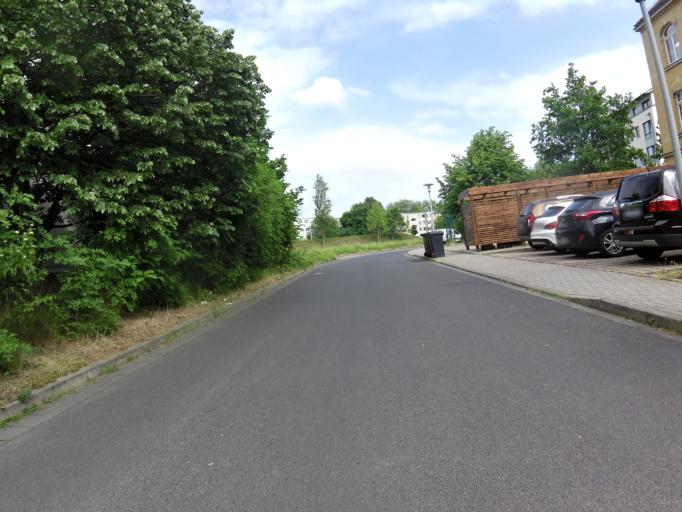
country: DE
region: Saxony
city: Leipzig
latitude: 51.3774
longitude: 12.3574
